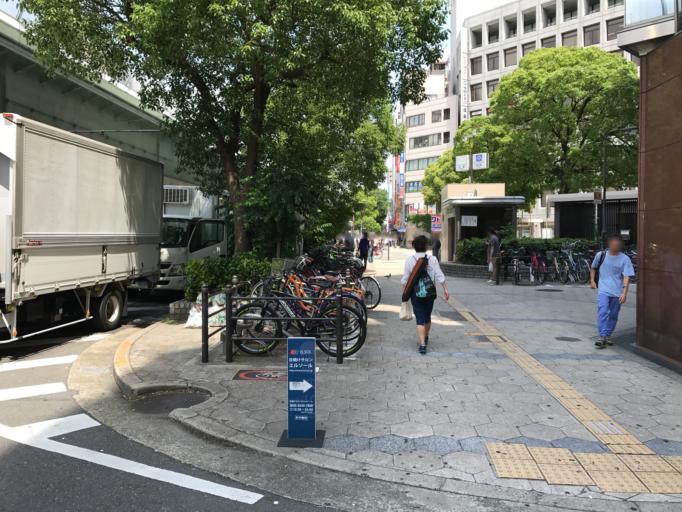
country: JP
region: Osaka
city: Osaka-shi
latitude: 34.6668
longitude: 135.5057
